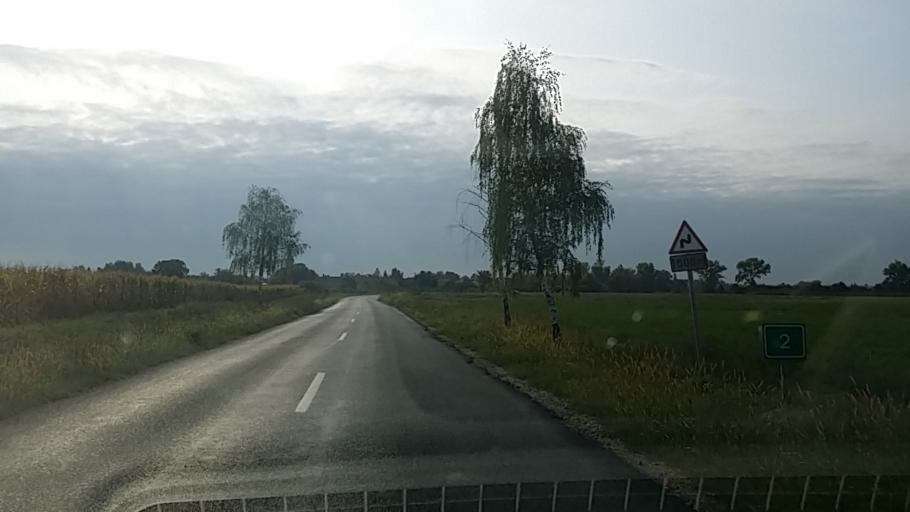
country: HU
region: Gyor-Moson-Sopron
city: Fertod
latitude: 47.6096
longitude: 16.8985
